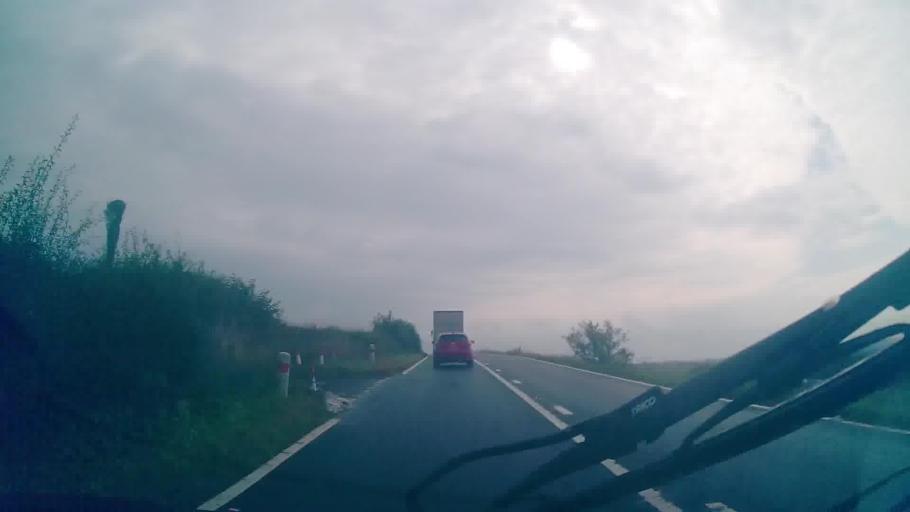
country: GB
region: Scotland
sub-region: Dumfries and Galloway
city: Lochmaben
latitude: 55.0553
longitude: -3.4701
